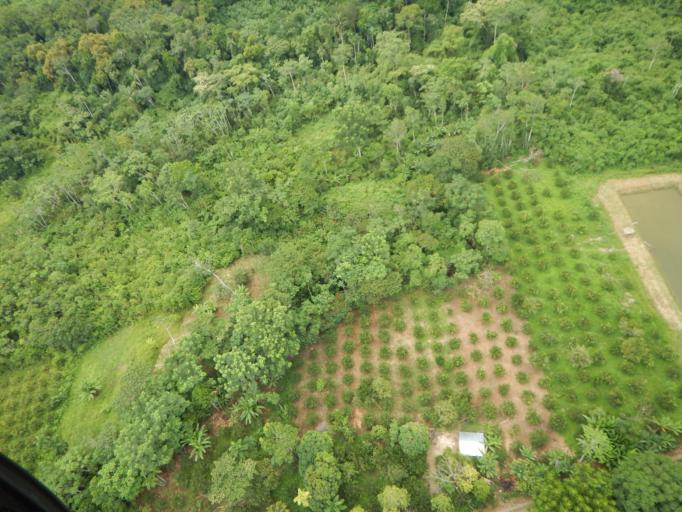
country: BO
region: Cochabamba
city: Chimore
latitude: -16.9977
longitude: -65.0855
